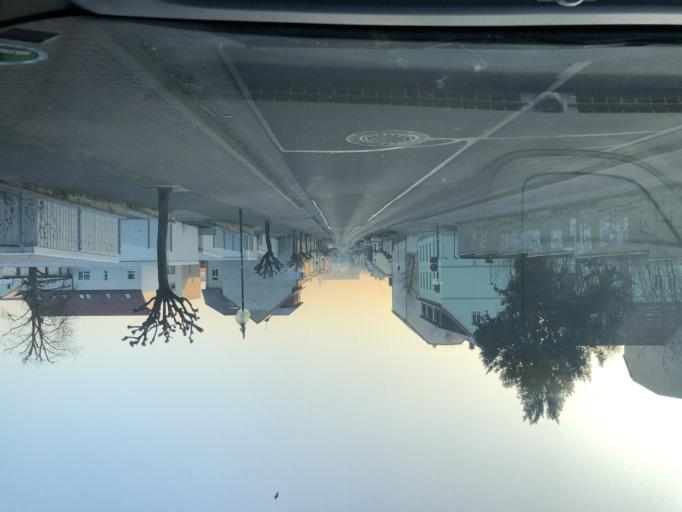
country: DE
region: Saxony
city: Schkeuditz
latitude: 51.4016
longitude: 12.2210
